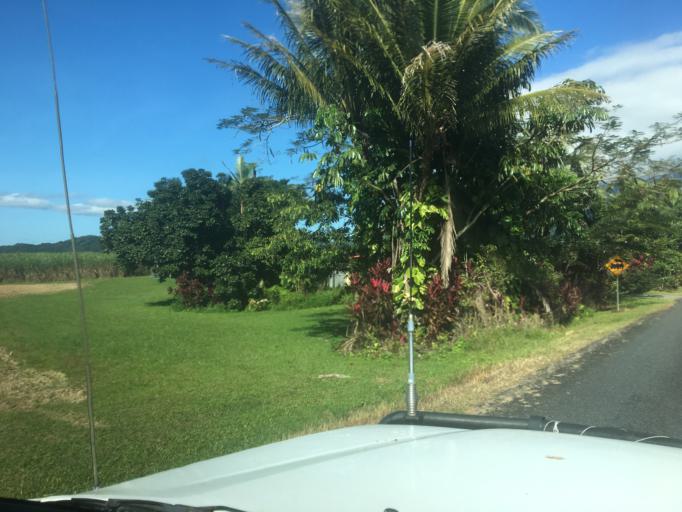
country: AU
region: Queensland
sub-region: Cassowary Coast
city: Innisfail
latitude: -17.3495
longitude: 145.9011
